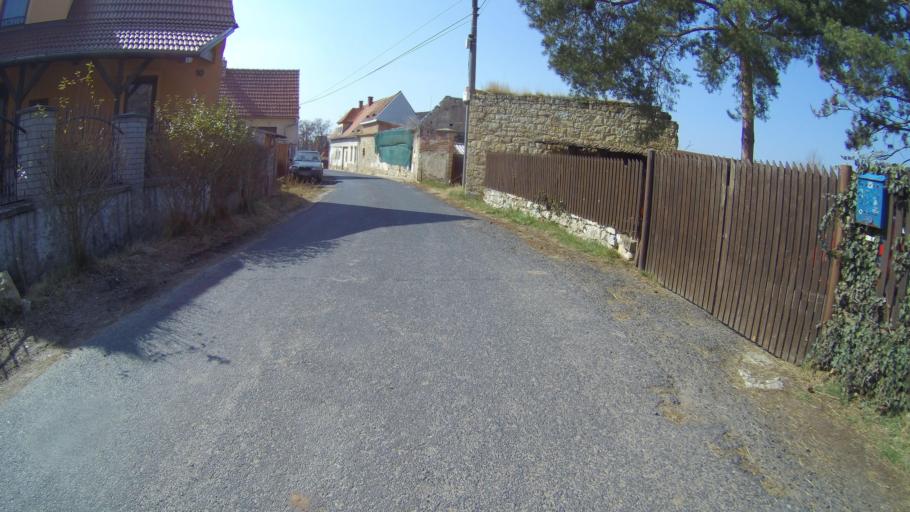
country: CZ
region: Ustecky
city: Mecholupy
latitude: 50.2894
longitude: 13.5790
